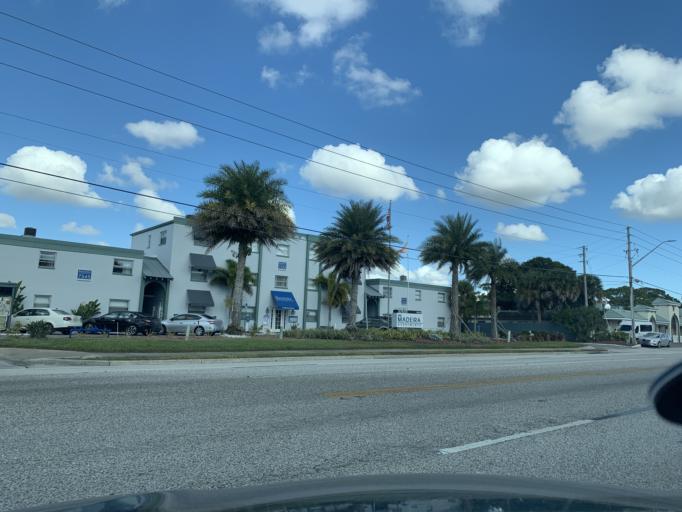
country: US
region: Florida
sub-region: Pinellas County
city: Kenneth City
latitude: 27.8063
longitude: -82.7433
